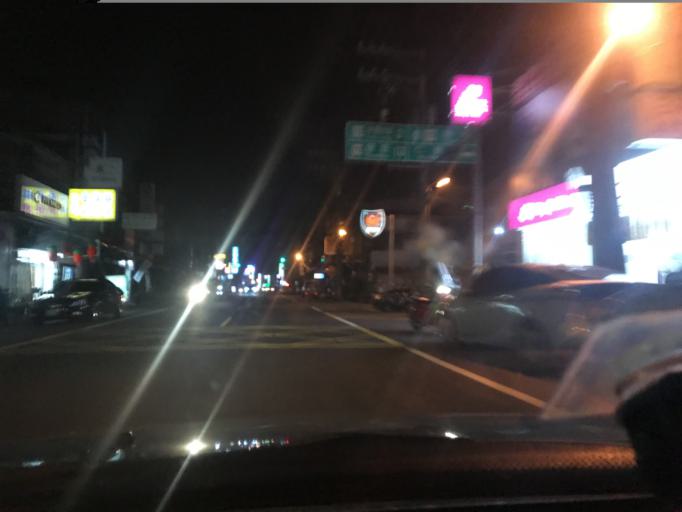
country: TW
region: Taiwan
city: Daxi
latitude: 24.9235
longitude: 121.2477
